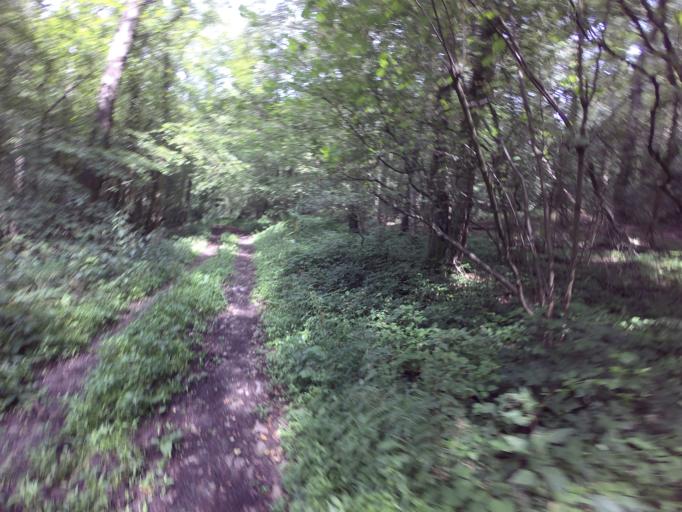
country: BE
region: Wallonia
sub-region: Province de Liege
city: Plombieres
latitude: 50.7553
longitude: 5.9795
